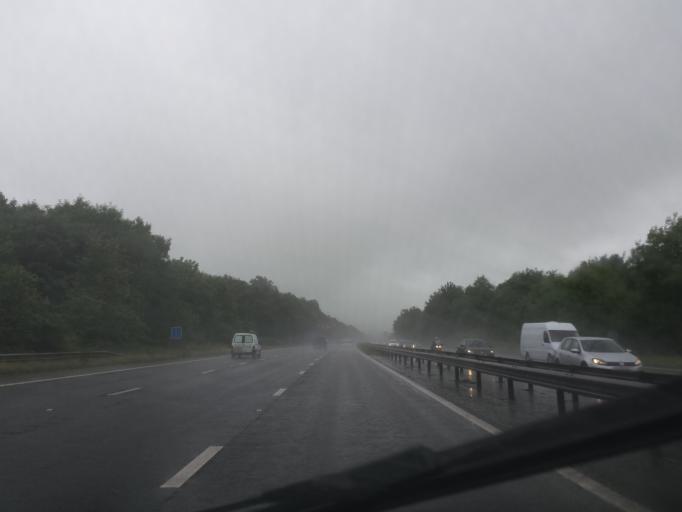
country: GB
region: England
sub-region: Leicestershire
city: Shepshed
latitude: 52.7523
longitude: -1.2747
